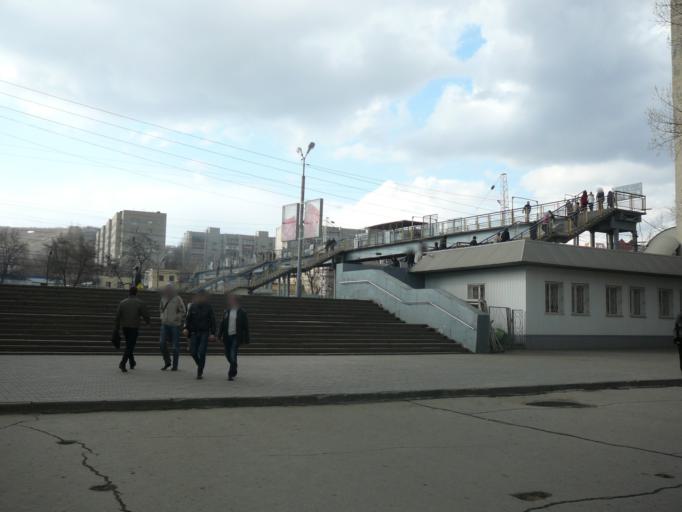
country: RU
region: Saratov
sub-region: Saratovskiy Rayon
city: Saratov
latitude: 51.5422
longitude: 45.9997
